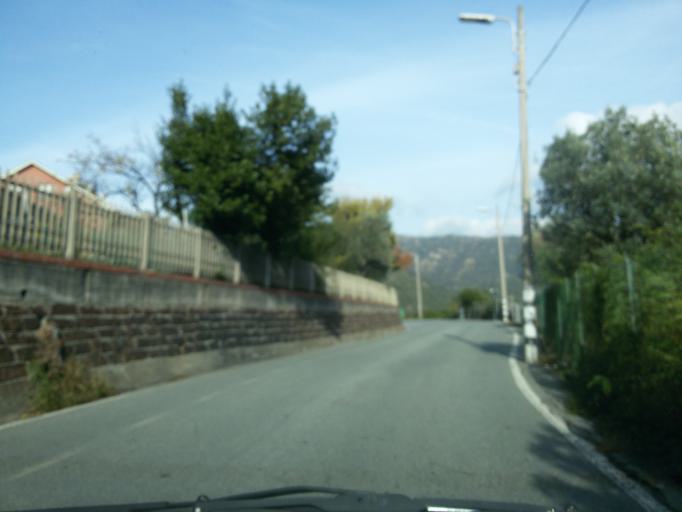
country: IT
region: Liguria
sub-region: Provincia di Genova
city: Piccarello
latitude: 44.4591
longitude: 8.9721
